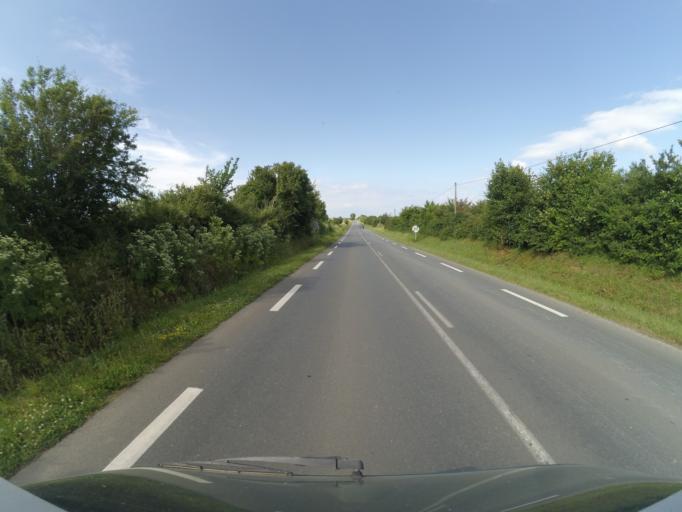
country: FR
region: Poitou-Charentes
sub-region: Departement de la Charente-Maritime
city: Saint-Xandre
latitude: 46.2279
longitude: -1.0806
